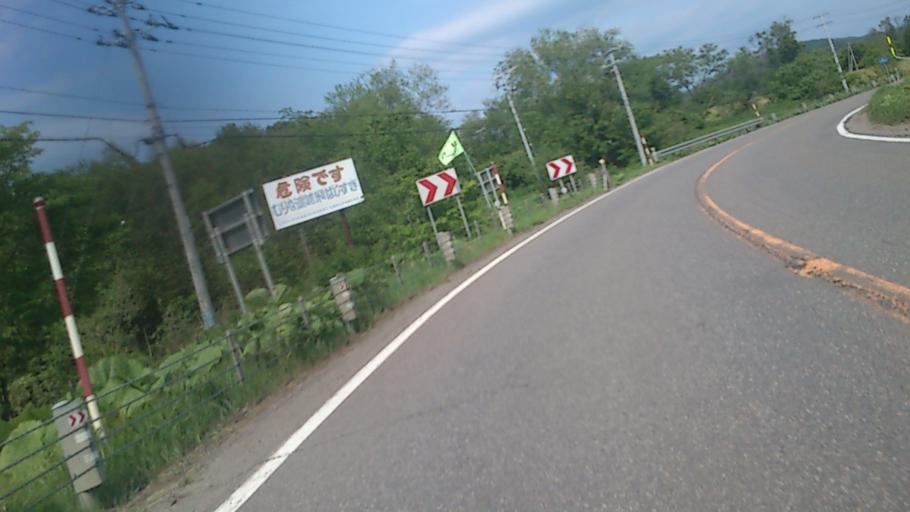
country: JP
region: Hokkaido
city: Kitami
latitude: 43.3038
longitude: 143.6882
